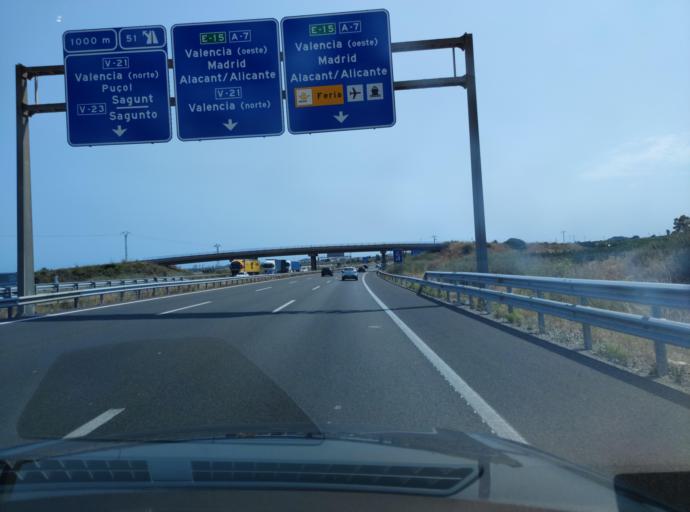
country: ES
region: Valencia
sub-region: Provincia de Valencia
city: Pucol
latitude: 39.6440
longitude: -0.3003
